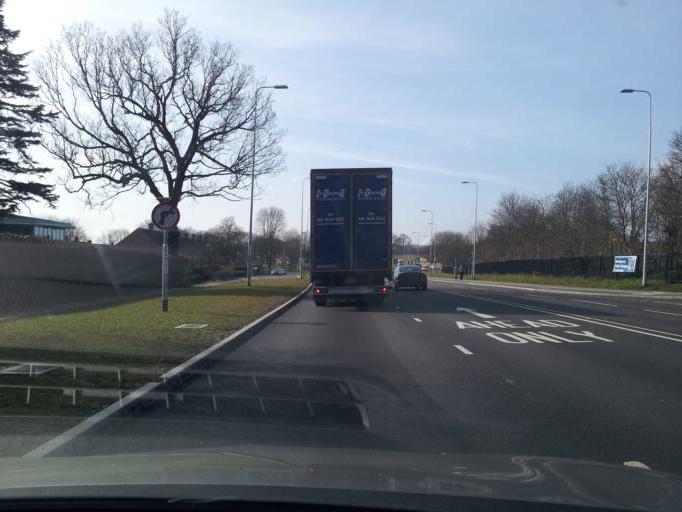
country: GB
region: England
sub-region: Nottinghamshire
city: Ruddington
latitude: 52.9091
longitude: -1.1847
